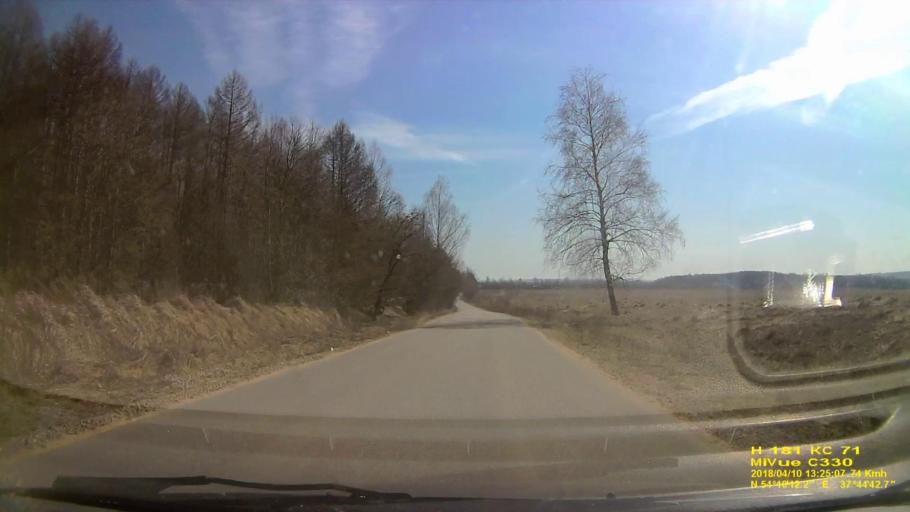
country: RU
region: Tula
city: Bolokhovo
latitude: 54.1700
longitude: 37.7452
